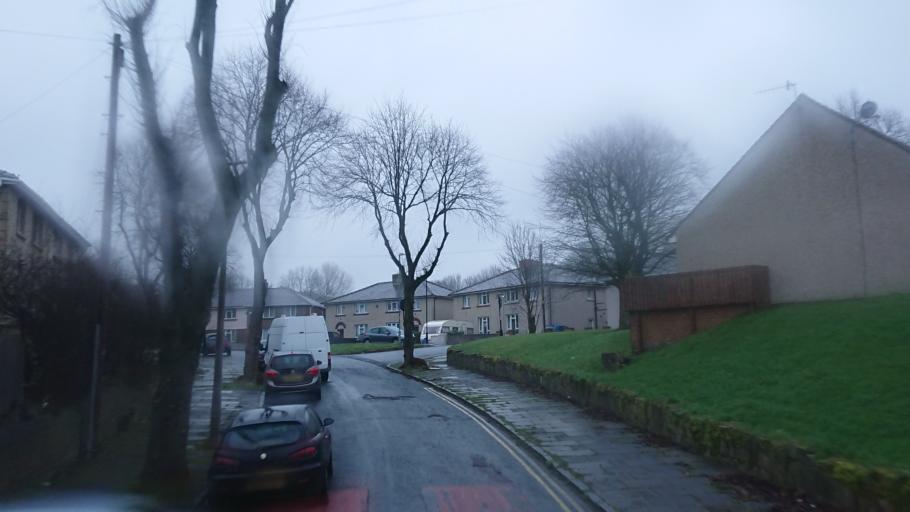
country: GB
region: England
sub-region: Lancashire
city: Lancaster
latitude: 54.0577
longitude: -2.7905
